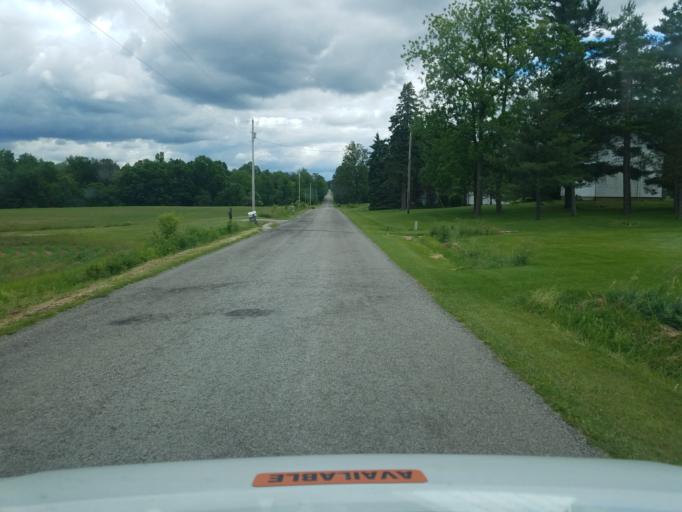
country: US
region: Ohio
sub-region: Crawford County
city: Galion
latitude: 40.6820
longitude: -82.7030
